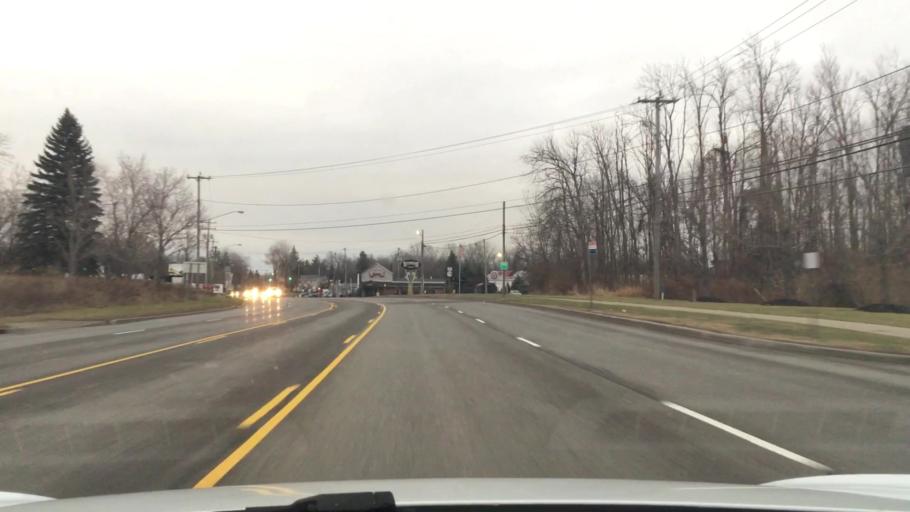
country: US
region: New York
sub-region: Erie County
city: Depew
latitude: 42.9372
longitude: -78.7001
